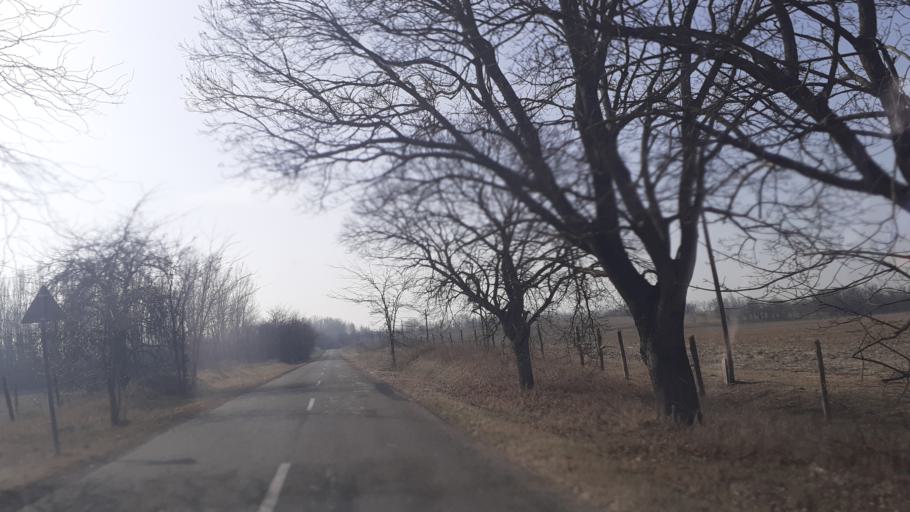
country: HU
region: Pest
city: Orkeny
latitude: 47.0513
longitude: 19.3275
